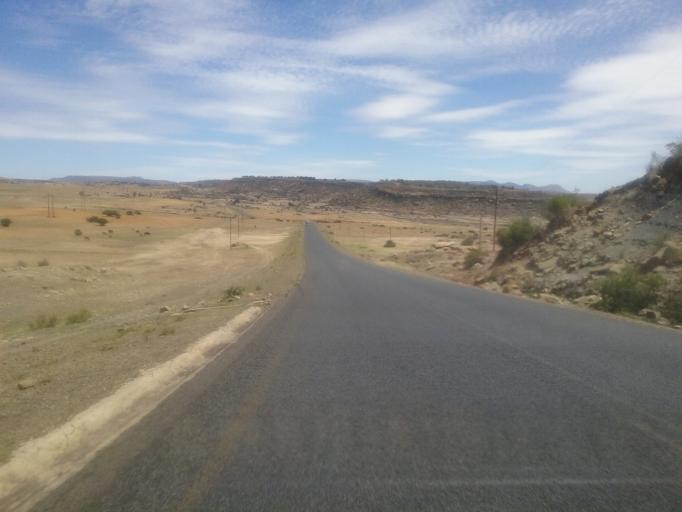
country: LS
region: Mohale's Hoek District
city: Mohale's Hoek
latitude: -30.0605
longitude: 27.4142
